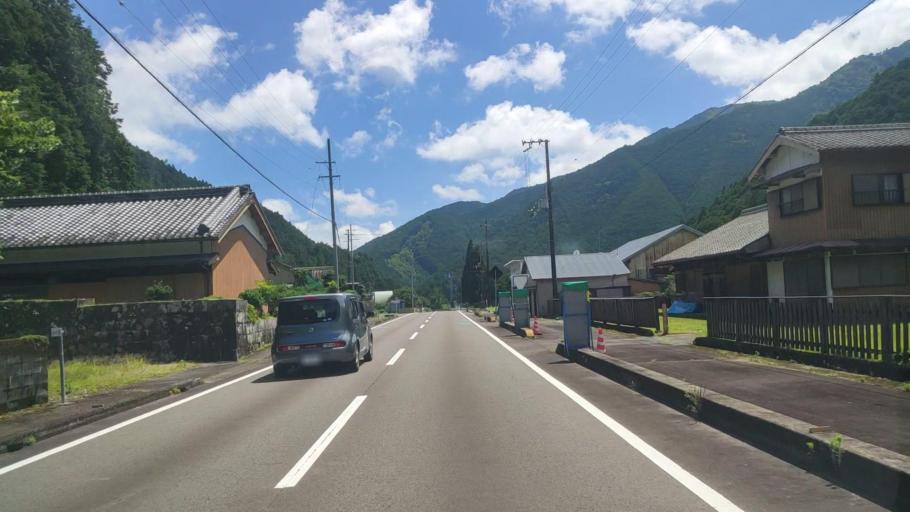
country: JP
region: Mie
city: Owase
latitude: 33.9790
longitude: 136.1047
